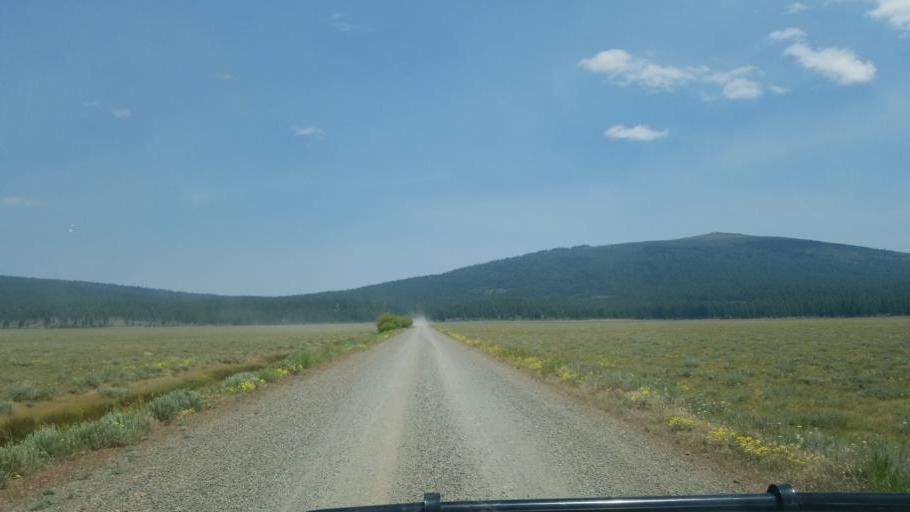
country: US
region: California
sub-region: Lassen County
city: Westwood
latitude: 40.5907
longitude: -120.9749
